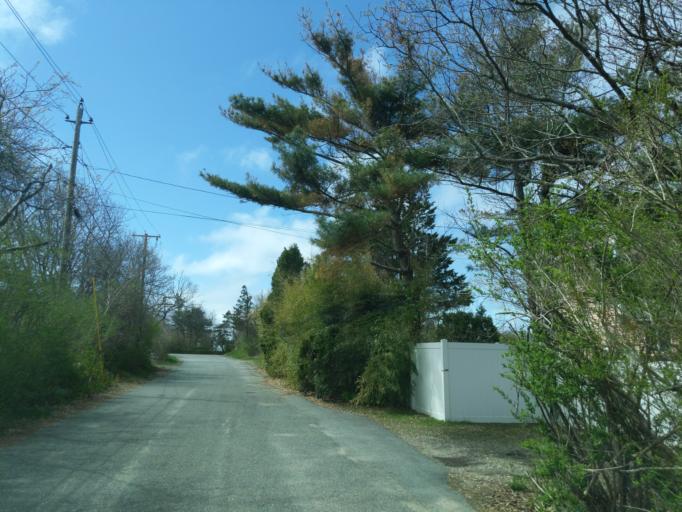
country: US
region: Massachusetts
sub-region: Essex County
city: Rockport
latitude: 42.6370
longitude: -70.5969
